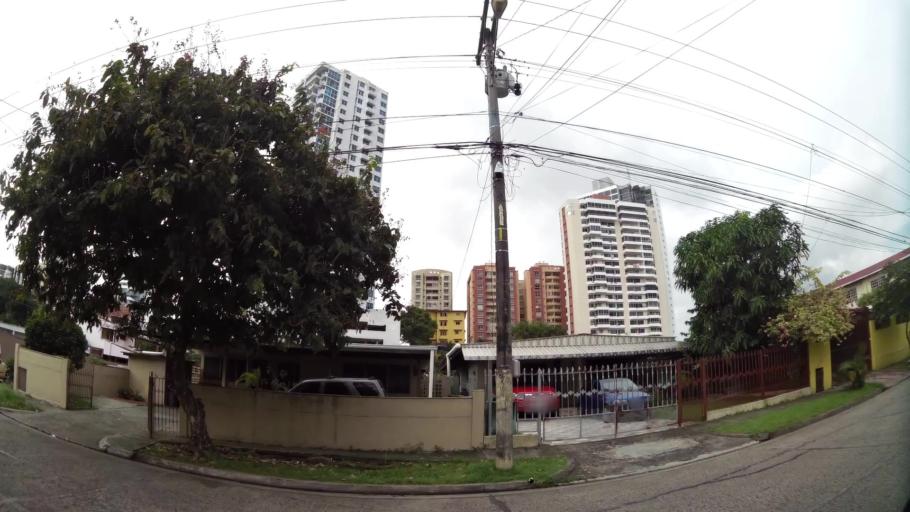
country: PA
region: Panama
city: Panama
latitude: 9.0163
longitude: -79.5320
